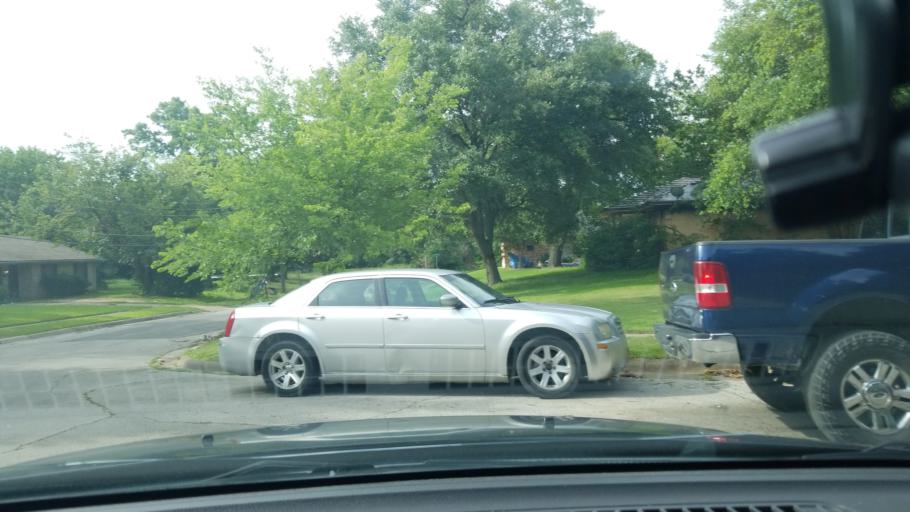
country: US
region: Texas
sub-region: Dallas County
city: Balch Springs
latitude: 32.7624
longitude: -96.6694
